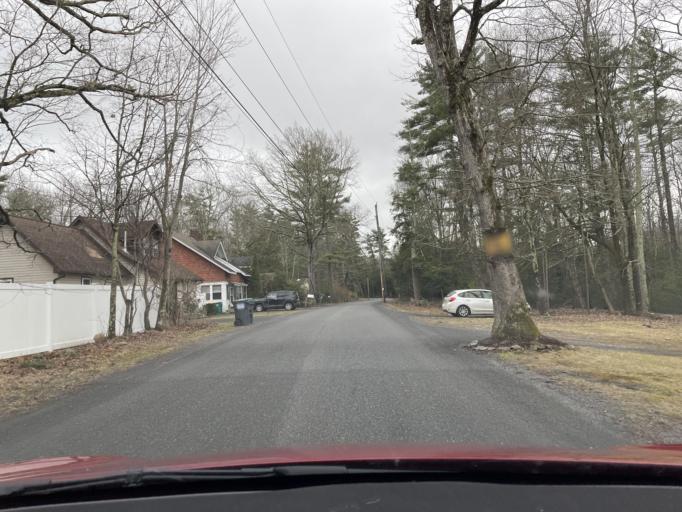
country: US
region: New York
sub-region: Ulster County
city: Manorville
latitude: 42.0961
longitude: -74.0349
